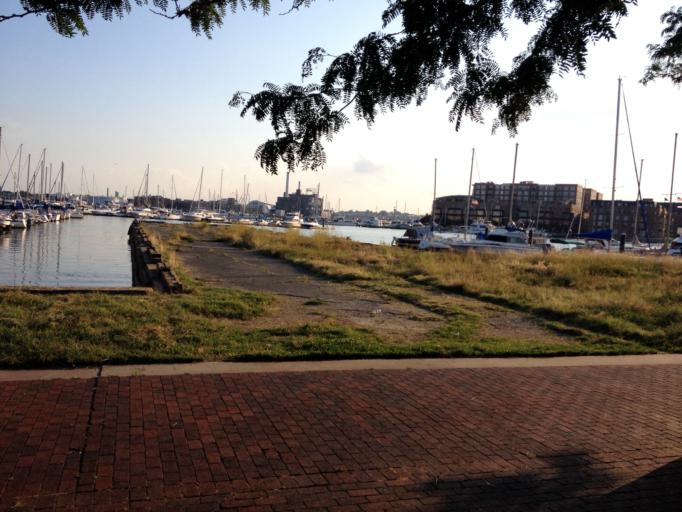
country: US
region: Maryland
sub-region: City of Baltimore
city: Baltimore
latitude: 39.2818
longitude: -76.5835
